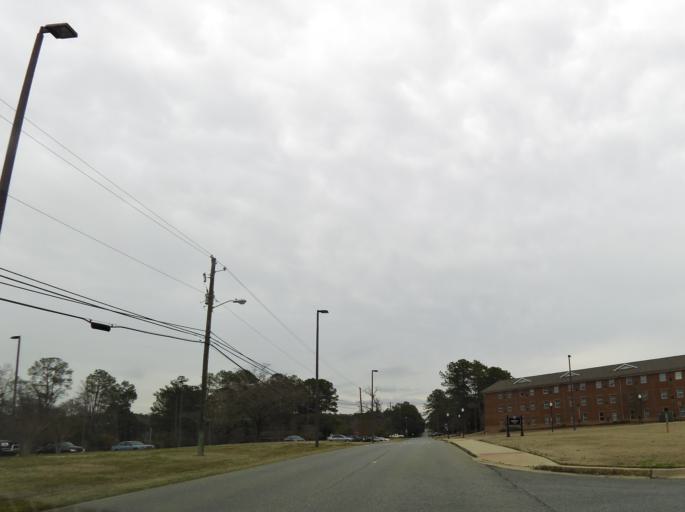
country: US
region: Georgia
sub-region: Bleckley County
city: Cochran
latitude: 32.3828
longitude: -83.3434
